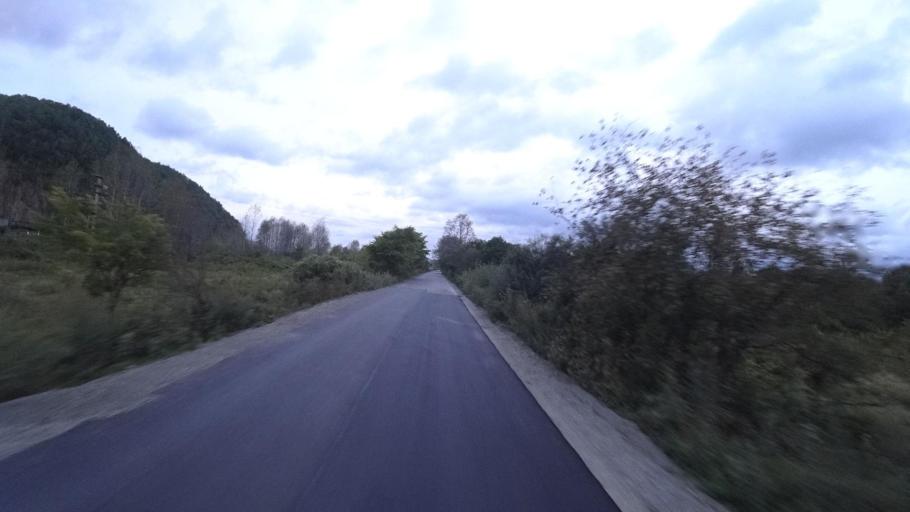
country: RU
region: Jewish Autonomous Oblast
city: Izvestkovyy
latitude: 48.9918
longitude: 131.5428
